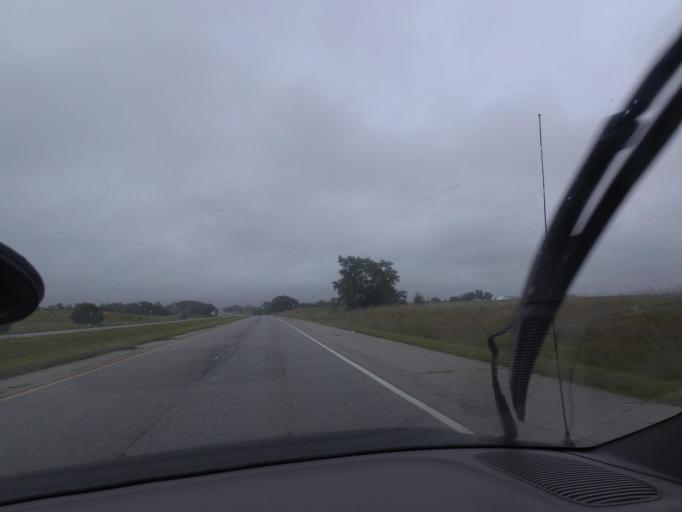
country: US
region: Illinois
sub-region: Pike County
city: Pittsfield
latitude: 39.6700
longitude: -90.8251
